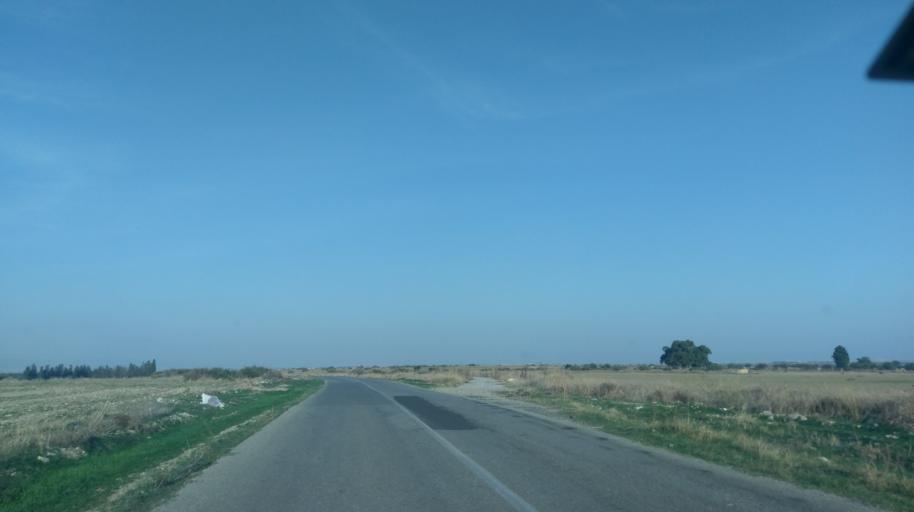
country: CY
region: Larnaka
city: Pergamos
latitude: 35.1186
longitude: 33.7305
